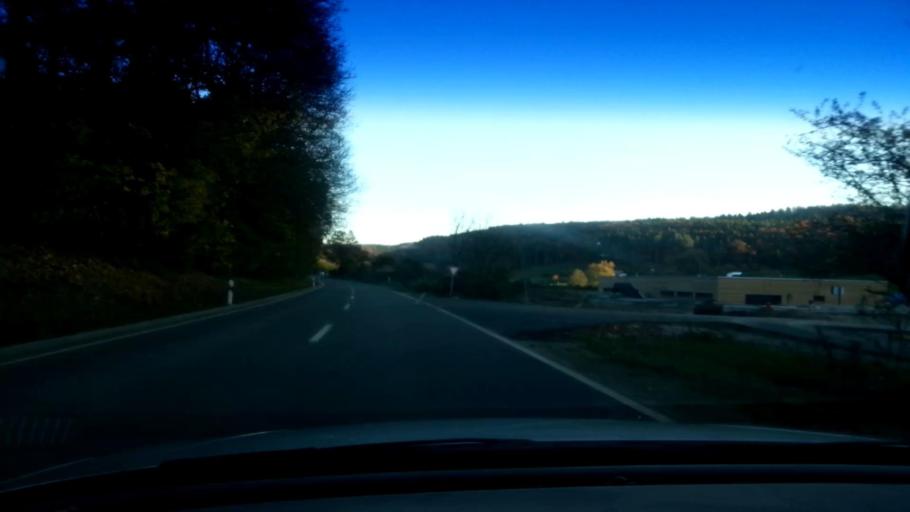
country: DE
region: Bavaria
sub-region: Upper Franconia
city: Heiligenstadt
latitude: 49.8527
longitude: 11.1822
